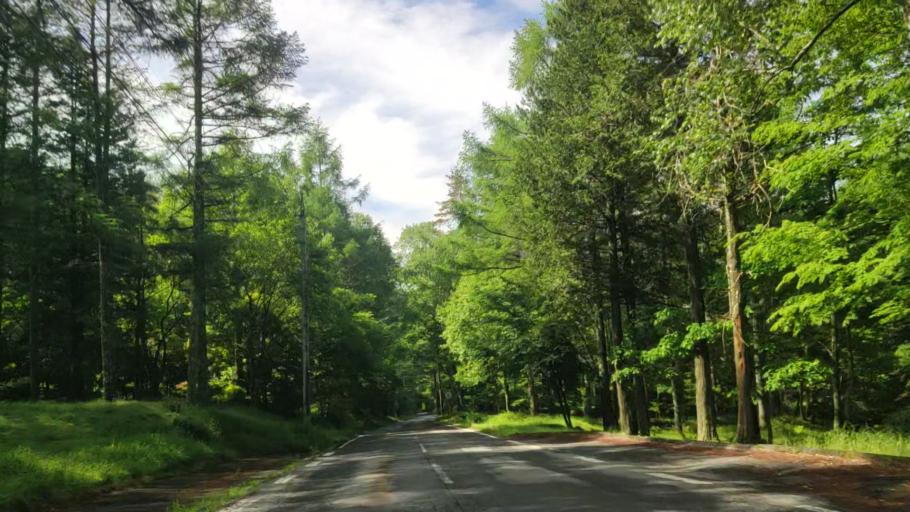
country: JP
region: Nagano
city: Suwa
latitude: 36.0872
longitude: 138.1437
